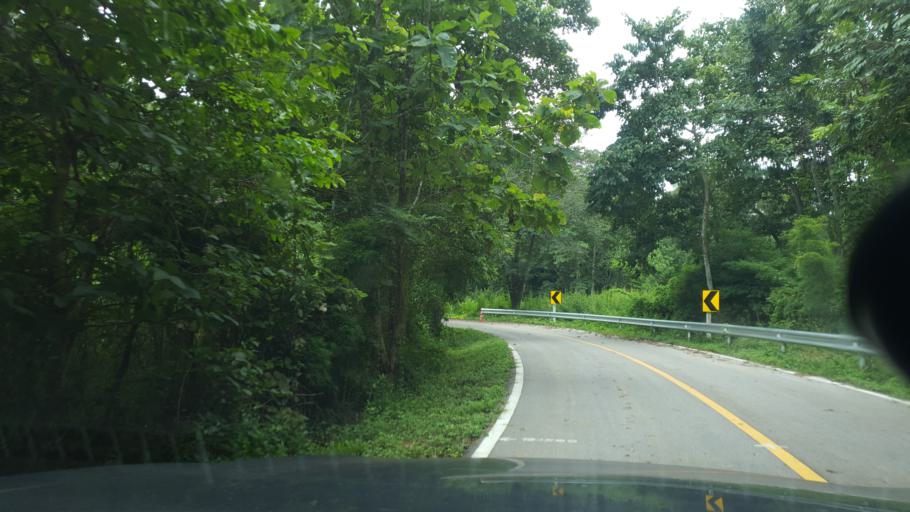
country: TH
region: Lamphun
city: Mae Tha
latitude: 18.4413
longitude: 99.2687
